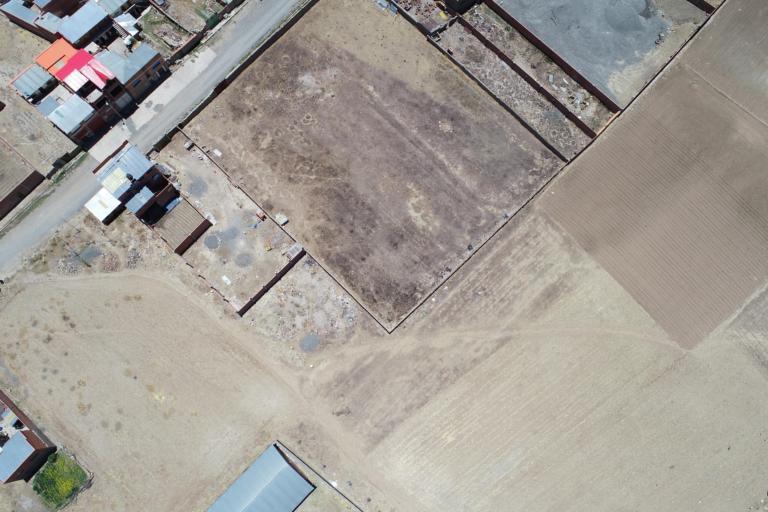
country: BO
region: La Paz
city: Achacachi
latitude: -16.0500
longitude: -68.6887
